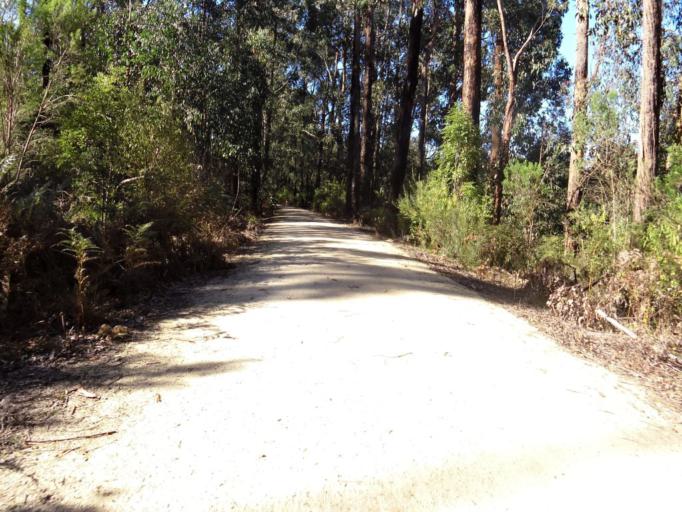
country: AU
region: Victoria
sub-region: Latrobe
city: Moe
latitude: -38.3877
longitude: 146.1883
